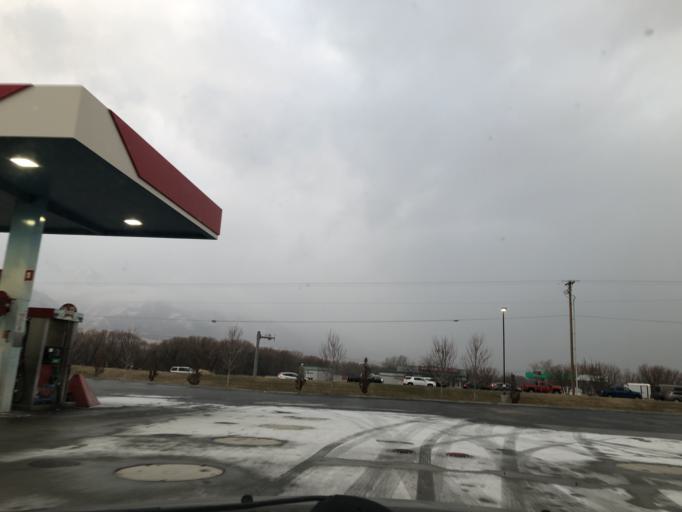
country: US
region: Utah
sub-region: Cache County
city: Wellsville
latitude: 41.6437
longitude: -111.9136
